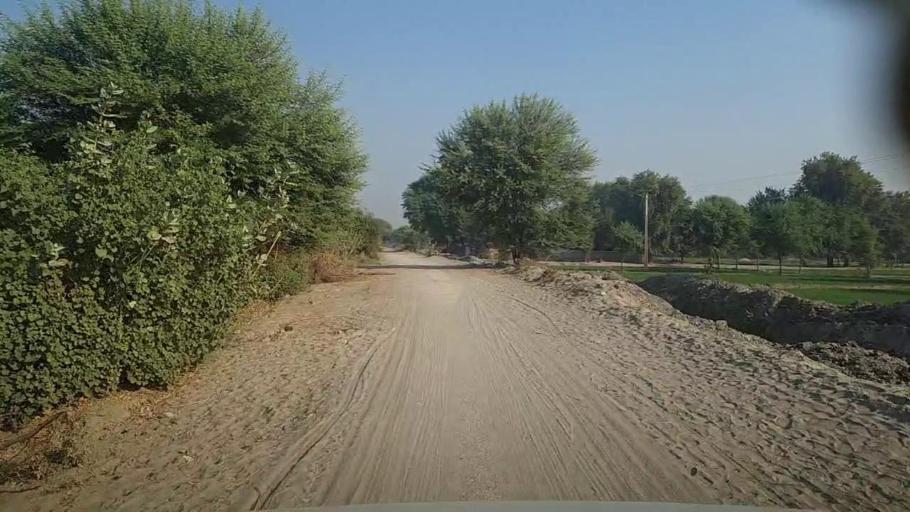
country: PK
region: Sindh
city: Karaundi
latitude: 26.7661
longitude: 68.4745
